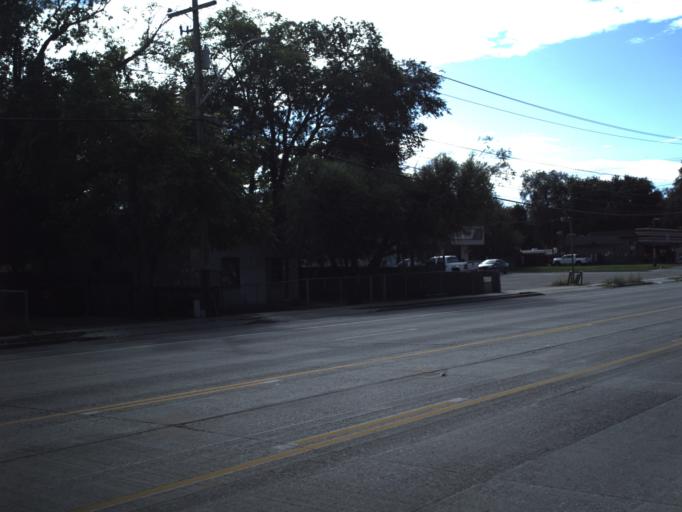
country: US
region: Utah
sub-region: Salt Lake County
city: Salt Lake City
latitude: 40.7811
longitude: -111.9395
